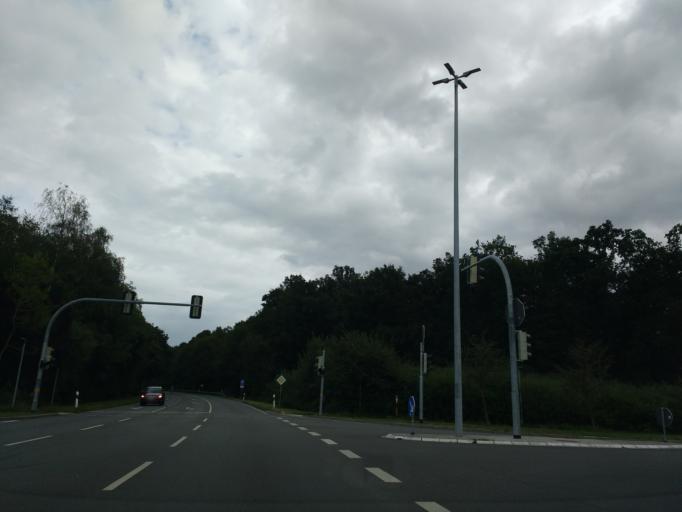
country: DE
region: Lower Saxony
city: Bad Rothenfelde
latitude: 52.1013
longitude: 8.1581
